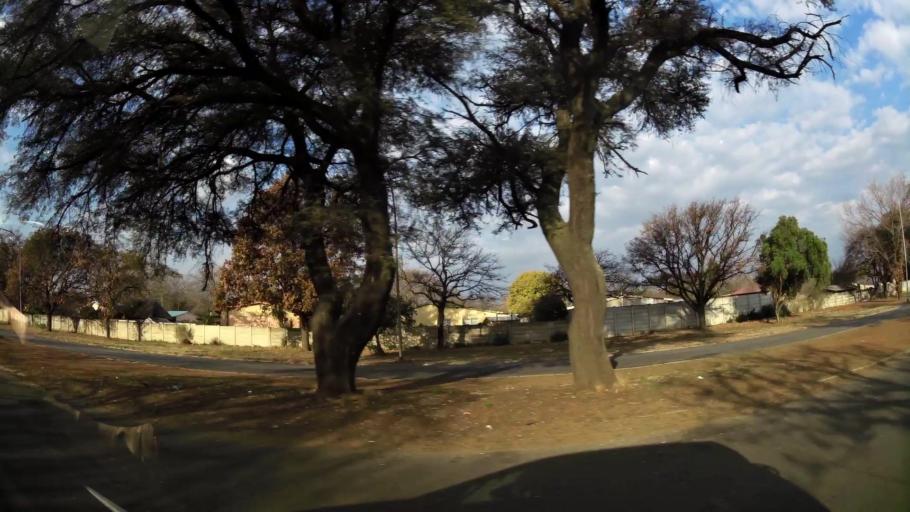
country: ZA
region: Orange Free State
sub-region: Fezile Dabi District Municipality
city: Sasolburg
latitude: -26.8186
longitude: 27.8090
